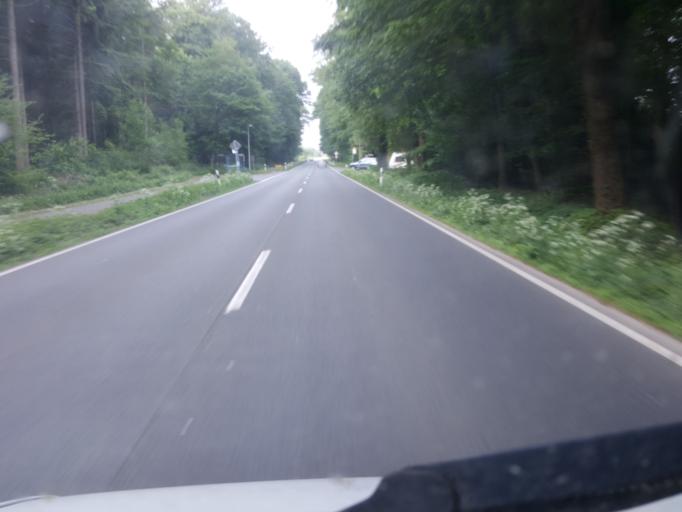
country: DE
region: Lower Saxony
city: Binnen
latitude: 52.6211
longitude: 9.1212
